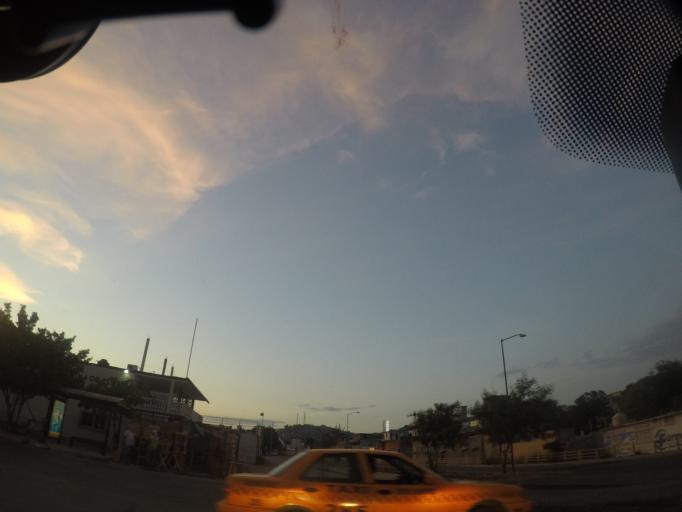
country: MX
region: Oaxaca
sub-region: Salina Cruz
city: Salina Cruz
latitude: 16.1785
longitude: -95.1955
